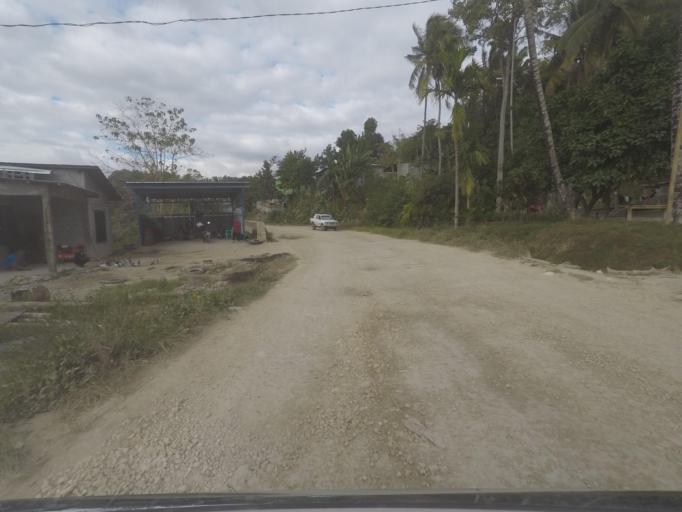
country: TL
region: Baucau
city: Venilale
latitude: -8.5995
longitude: 126.3861
